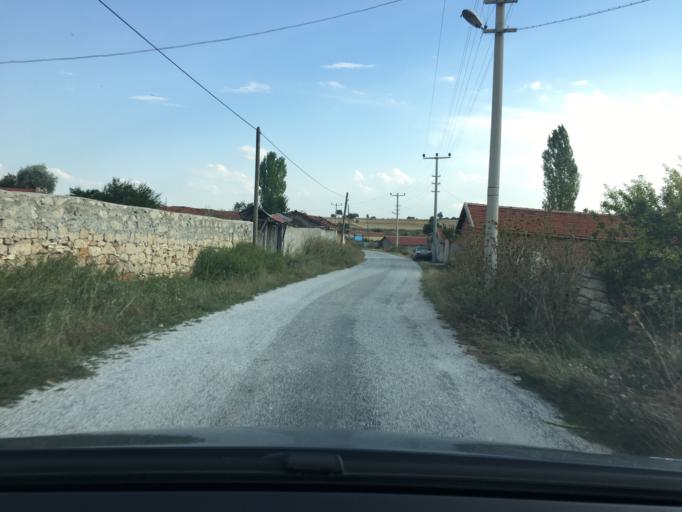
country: TR
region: Eskisehir
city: Kirka
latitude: 39.2748
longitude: 30.6768
